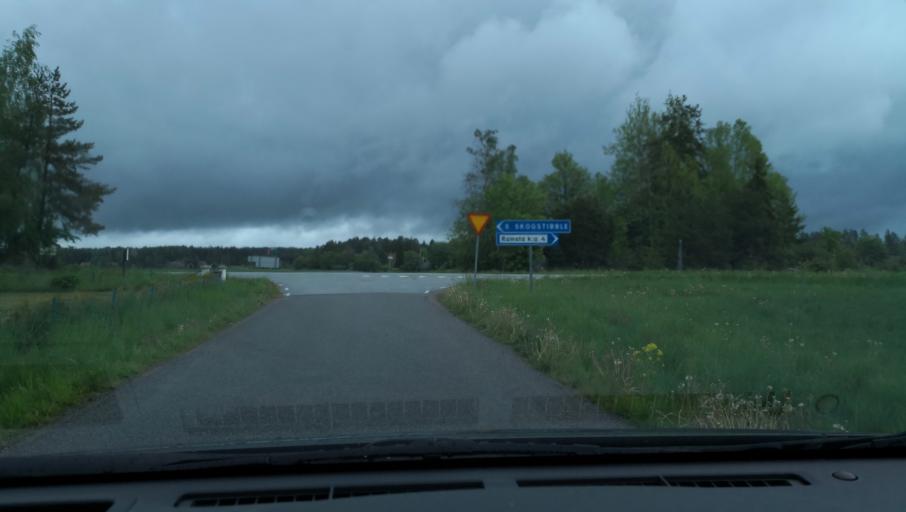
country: SE
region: Uppsala
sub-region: Enkopings Kommun
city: Orsundsbro
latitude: 59.8113
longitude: 17.3836
